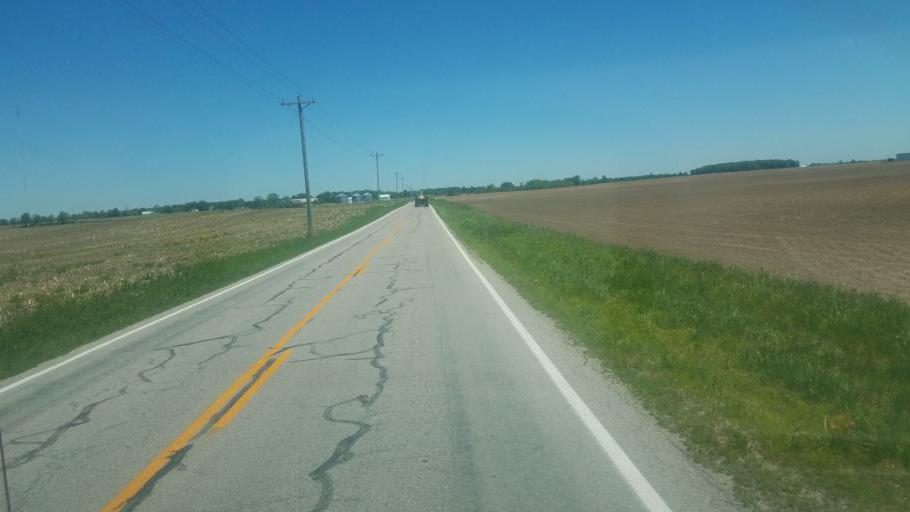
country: US
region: Ohio
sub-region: Miami County
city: Piqua
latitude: 40.2129
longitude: -84.3049
